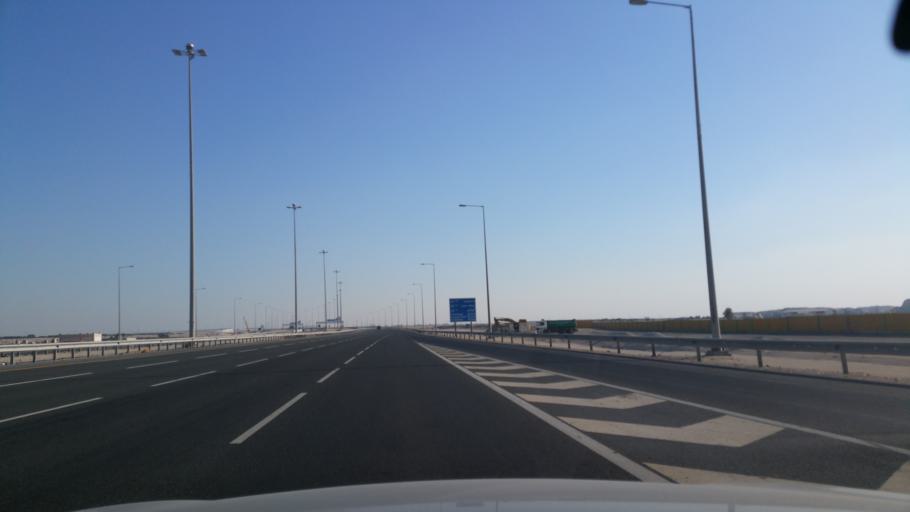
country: QA
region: Al Wakrah
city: Al Wukayr
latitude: 25.1493
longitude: 51.4742
